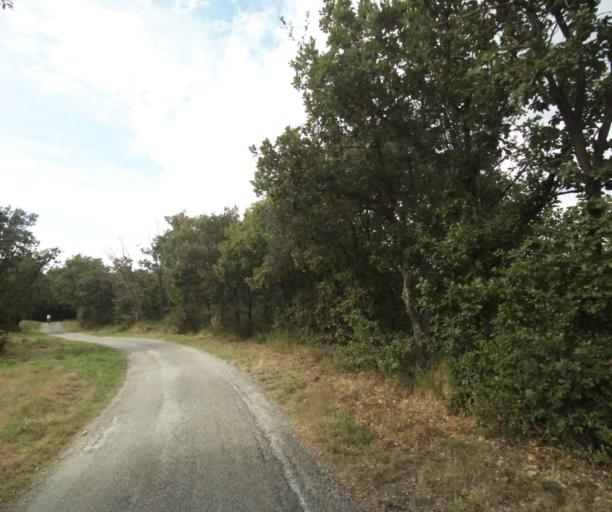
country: FR
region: Languedoc-Roussillon
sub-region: Departement des Pyrenees-Orientales
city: Argelers
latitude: 42.5326
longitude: 3.0204
